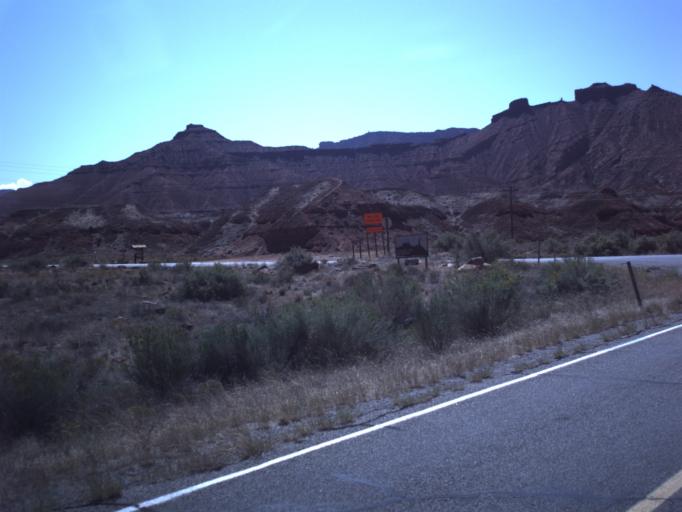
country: US
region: Utah
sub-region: Grand County
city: Moab
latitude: 38.6839
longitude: -109.4222
